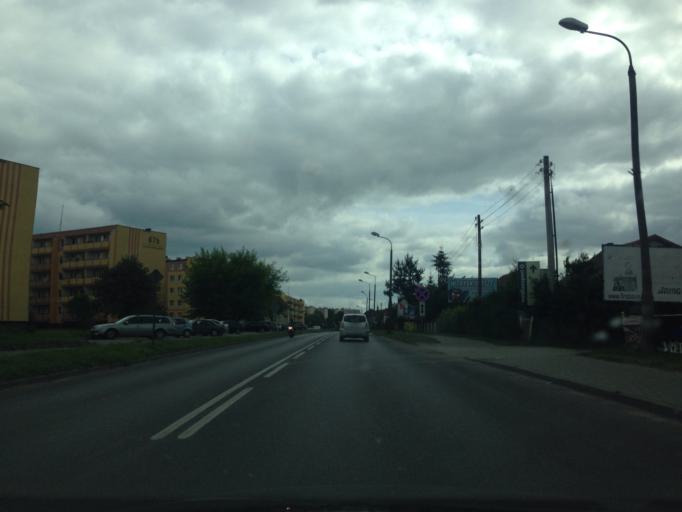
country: PL
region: Kujawsko-Pomorskie
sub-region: Powiat swiecki
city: Swiecie
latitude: 53.4042
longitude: 18.4223
